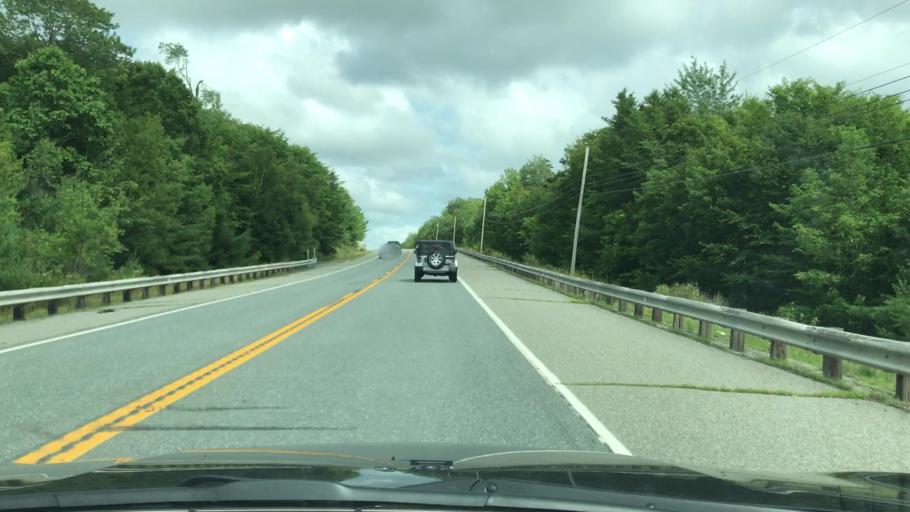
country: US
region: Maine
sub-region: Hancock County
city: Surry
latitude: 44.5648
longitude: -68.6041
